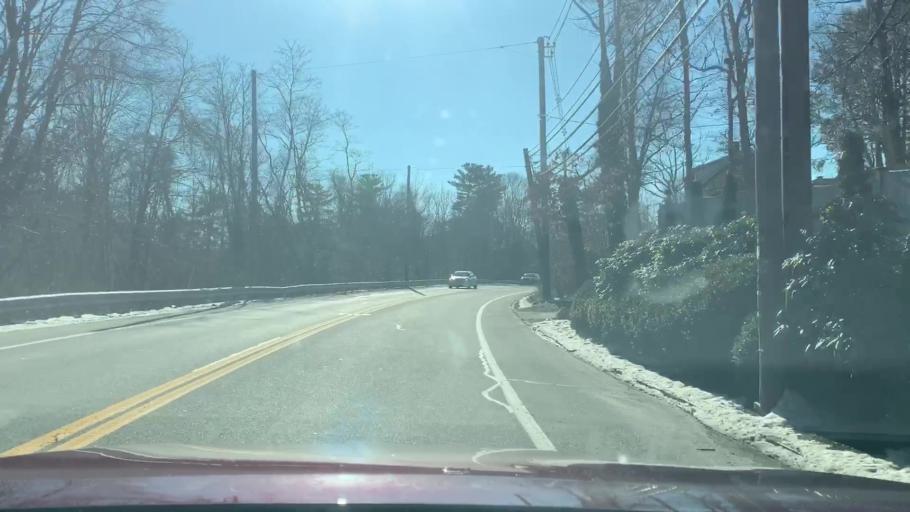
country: US
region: Massachusetts
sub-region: Essex County
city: Gloucester
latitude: 42.6132
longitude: -70.7012
